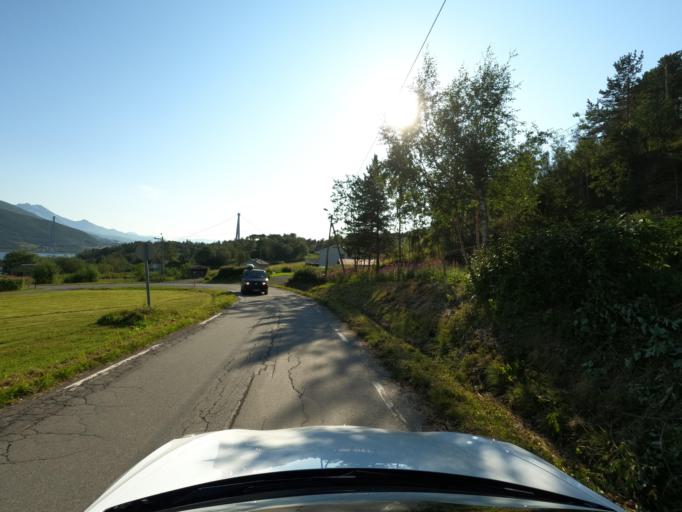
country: NO
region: Nordland
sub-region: Narvik
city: Narvik
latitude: 68.4717
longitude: 17.5040
